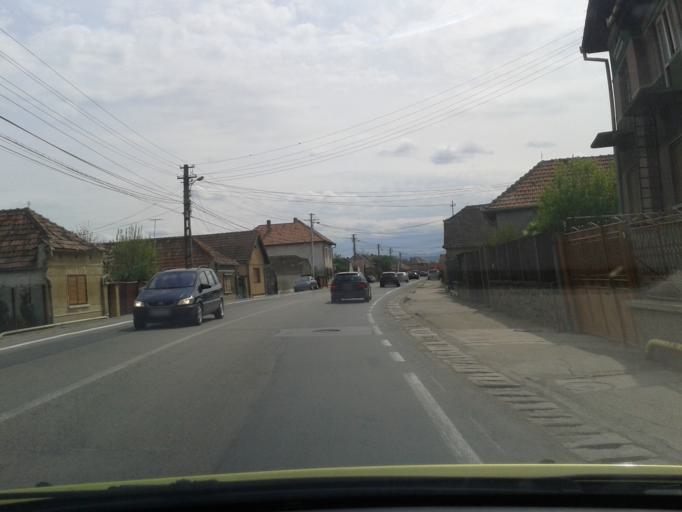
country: RO
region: Alba
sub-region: Municipiul Sebes
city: Lancram
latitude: 45.9828
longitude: 23.5558
